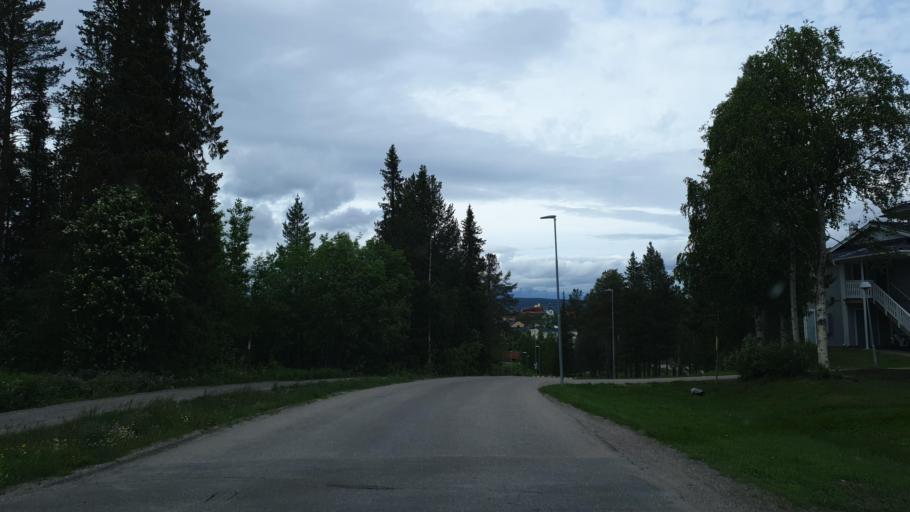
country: SE
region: Norrbotten
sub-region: Gallivare Kommun
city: Gaellivare
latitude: 67.1258
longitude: 20.6563
